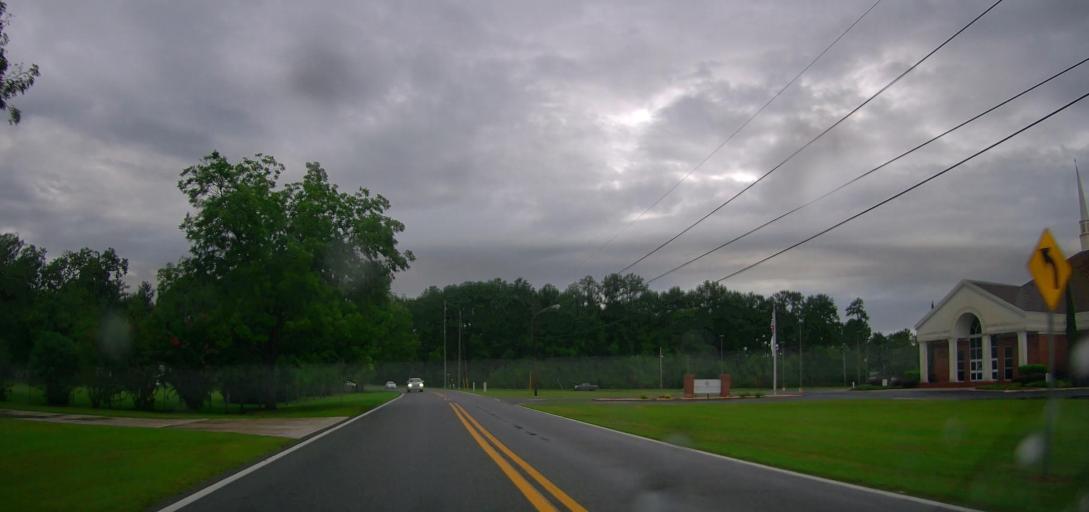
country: US
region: Georgia
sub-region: Ware County
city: Deenwood
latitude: 31.2358
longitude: -82.3789
